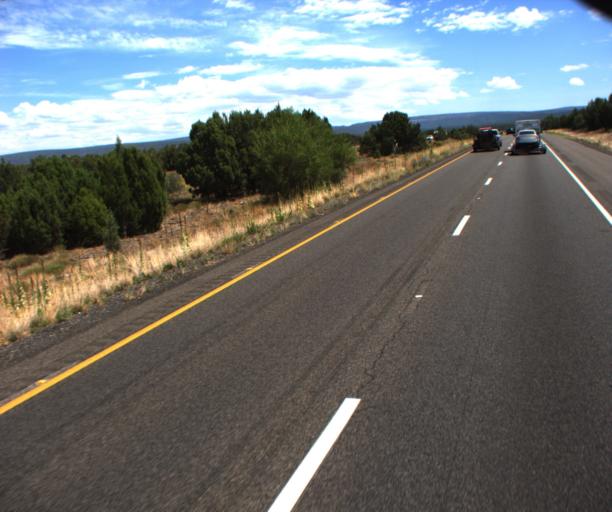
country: US
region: Arizona
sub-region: Yavapai County
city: Village of Oak Creek (Big Park)
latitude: 34.7567
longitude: -111.6667
